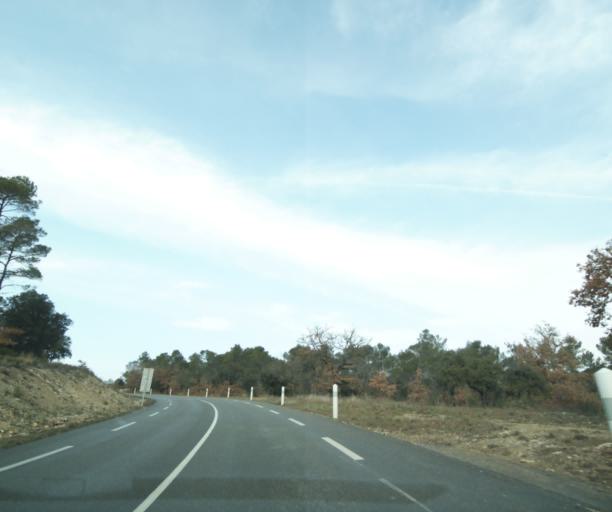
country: FR
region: Provence-Alpes-Cote d'Azur
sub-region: Departement du Var
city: Tourves
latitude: 43.4003
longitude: 5.9631
